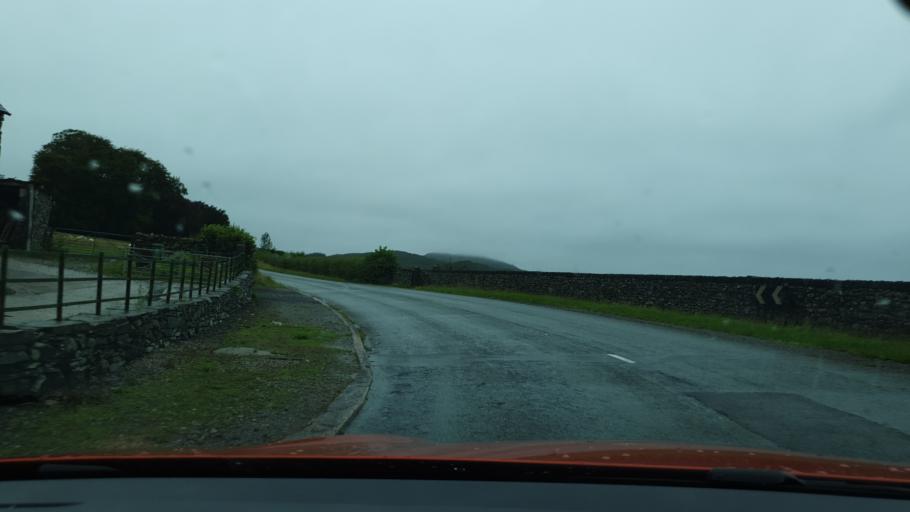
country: GB
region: England
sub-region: Cumbria
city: Ulverston
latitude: 54.2824
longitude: -3.0905
